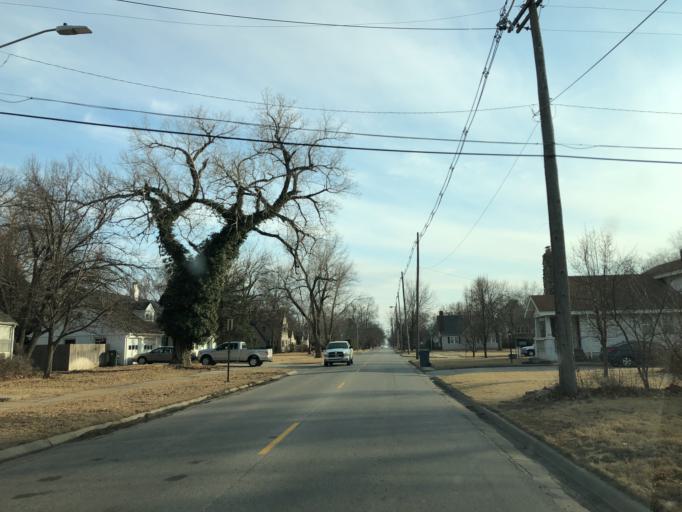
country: US
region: Kansas
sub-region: Reno County
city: Hutchinson
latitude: 38.0786
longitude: -97.9356
